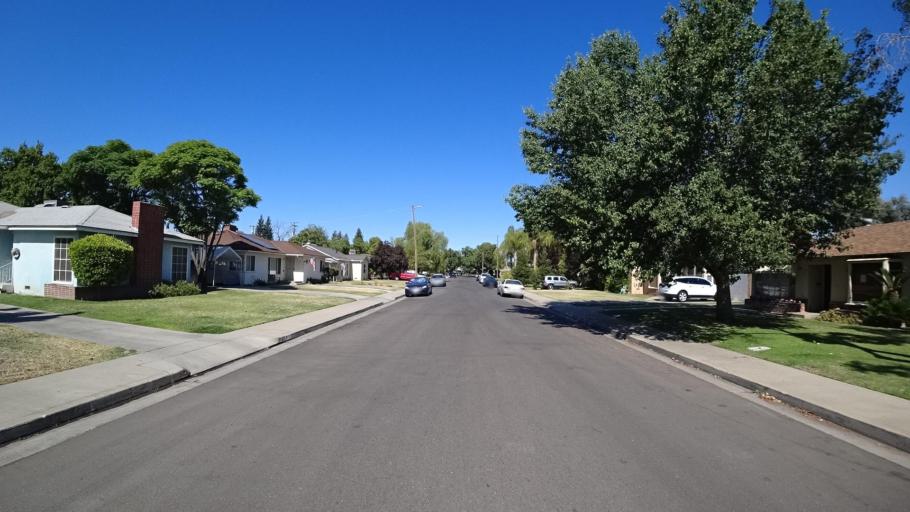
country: US
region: California
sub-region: Fresno County
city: Fresno
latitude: 36.7621
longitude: -119.8210
